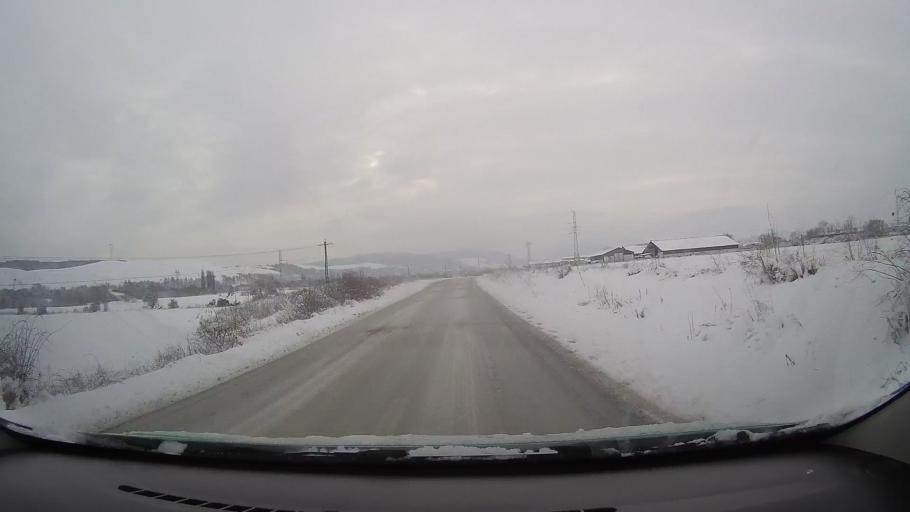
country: RO
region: Alba
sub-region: Comuna Pianu
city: Pianu de Jos
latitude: 45.9561
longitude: 23.4772
